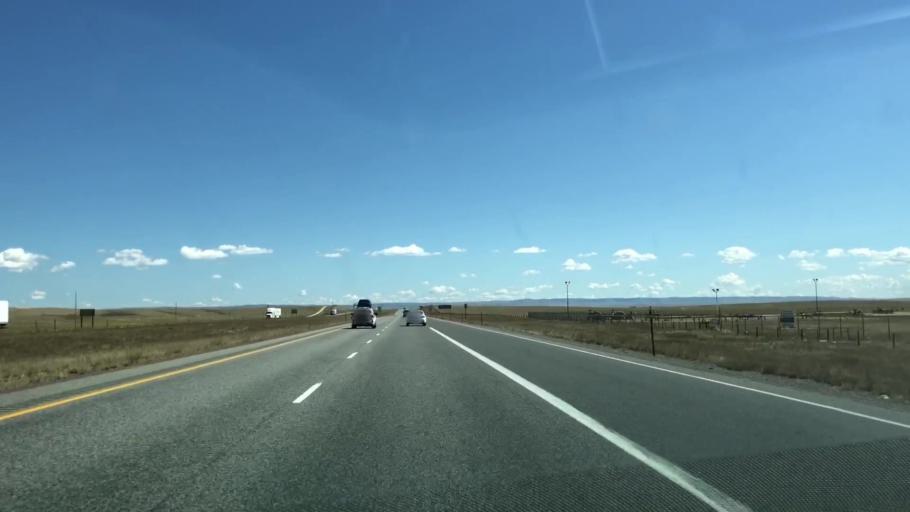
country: US
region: Wyoming
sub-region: Albany County
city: Laramie
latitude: 41.4390
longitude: -105.9370
